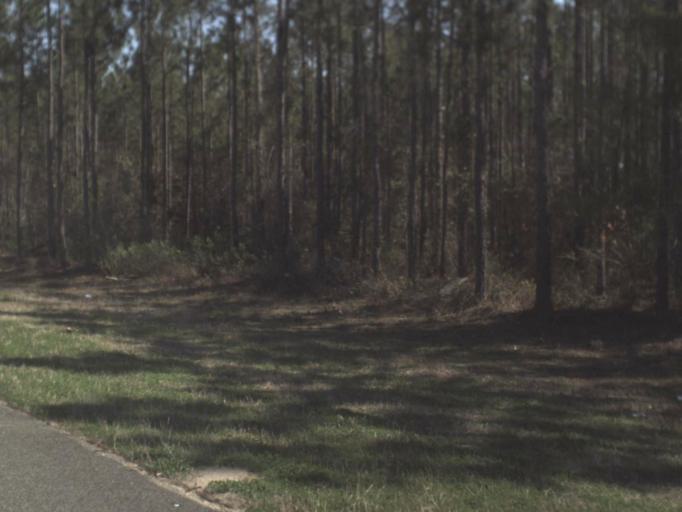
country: US
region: Florida
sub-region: Liberty County
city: Bristol
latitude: 30.4655
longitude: -84.9465
